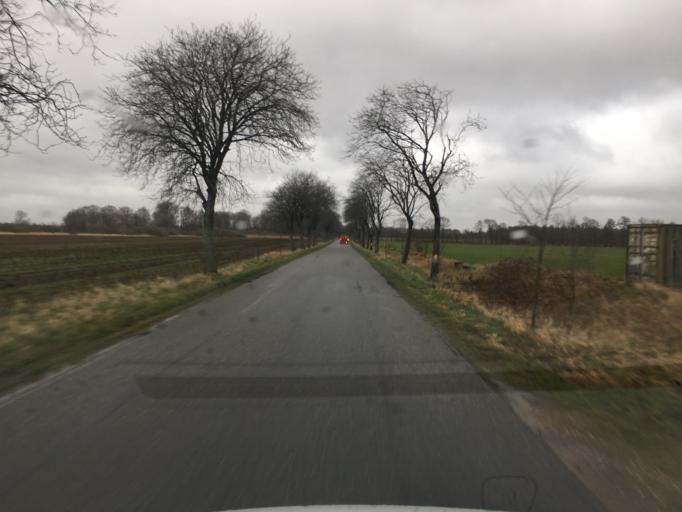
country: DK
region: South Denmark
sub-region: Aabenraa Kommune
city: Tinglev
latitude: 54.9021
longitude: 9.3066
